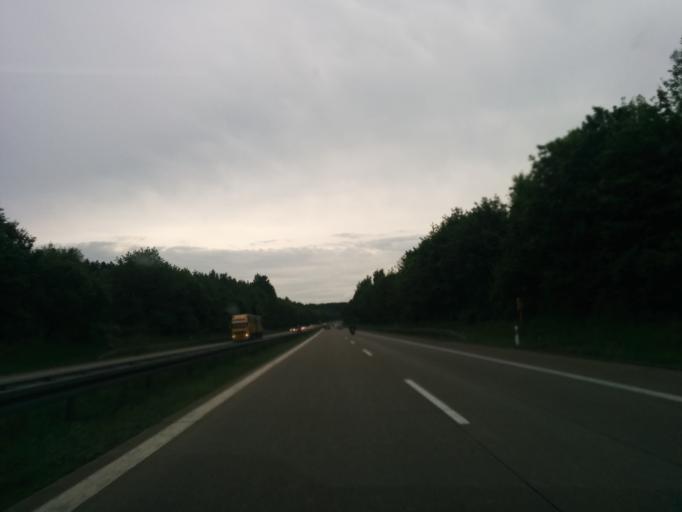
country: DE
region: Baden-Wuerttemberg
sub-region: Regierungsbezirk Stuttgart
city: Lauchheim
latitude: 48.7889
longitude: 10.2111
